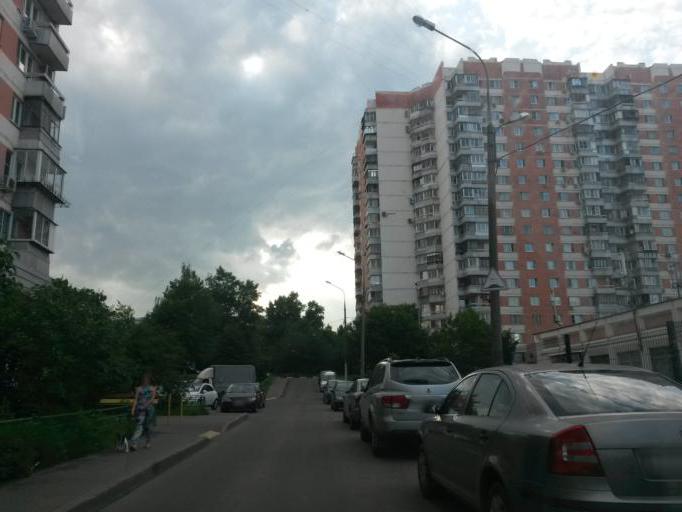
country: RU
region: Moscow
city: Annino
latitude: 55.5613
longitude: 37.5832
